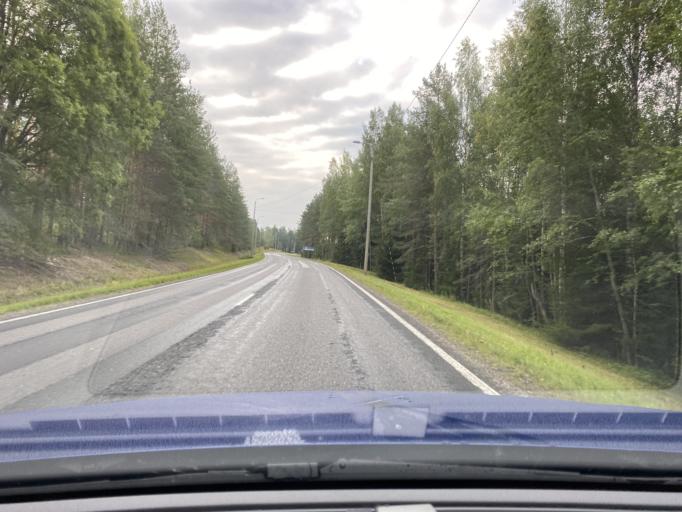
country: FI
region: Southern Ostrobothnia
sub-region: Seinaejoki
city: Jurva
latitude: 62.6783
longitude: 21.9778
